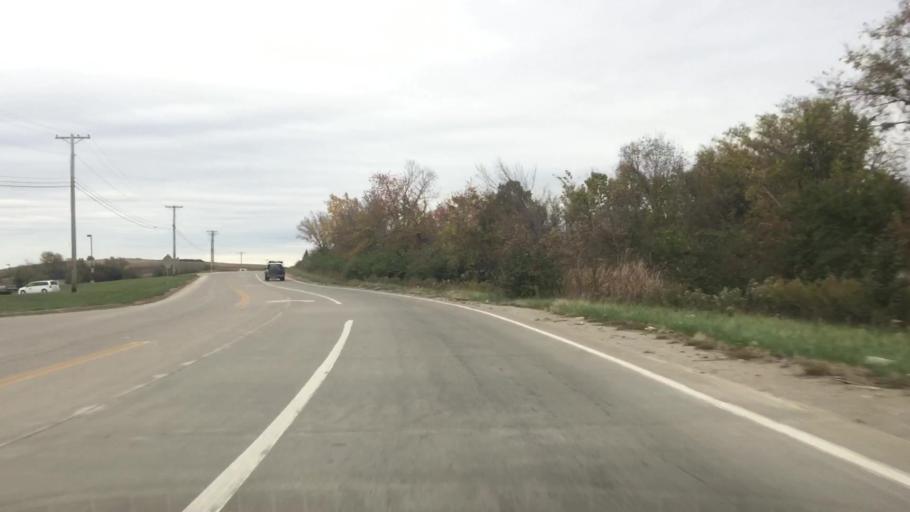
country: US
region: Missouri
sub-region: Jackson County
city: Lees Summit
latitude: 38.8845
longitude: -94.3594
